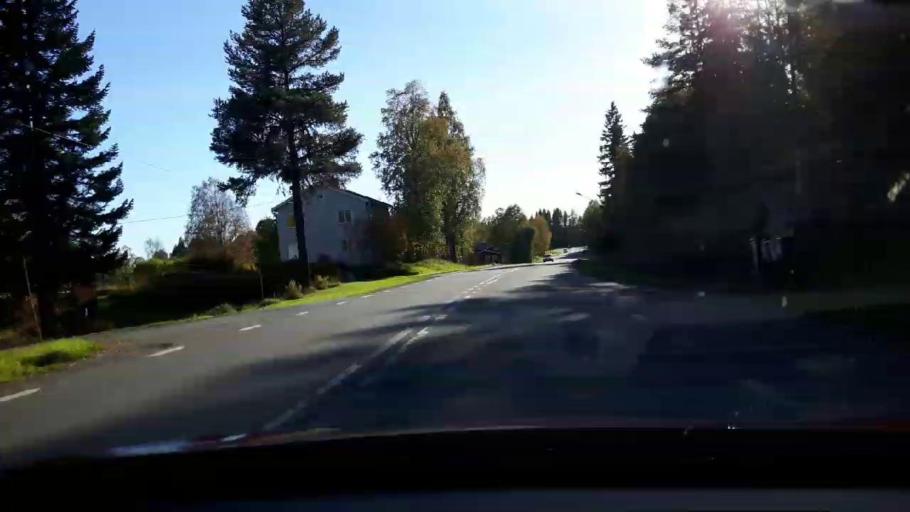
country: SE
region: Jaemtland
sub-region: Stroemsunds Kommun
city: Stroemsund
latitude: 63.8447
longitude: 15.5315
